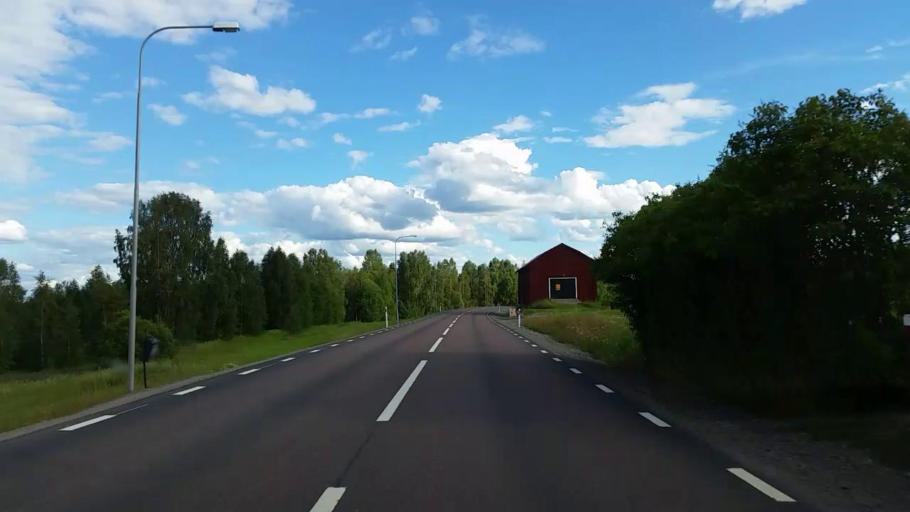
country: SE
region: Gaevleborg
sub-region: Ljusdals Kommun
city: Ljusdal
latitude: 61.8451
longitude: 16.0019
